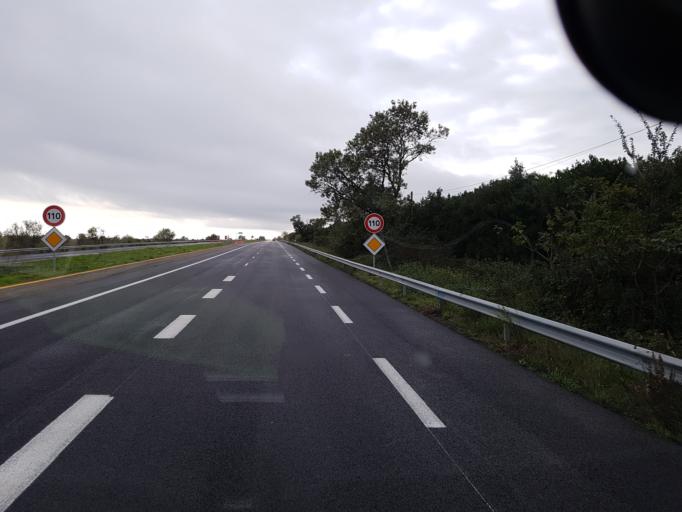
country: FR
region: Provence-Alpes-Cote d'Azur
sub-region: Departement des Bouches-du-Rhone
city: Saint-Martin-de-Crau
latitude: 43.6244
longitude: 4.7490
